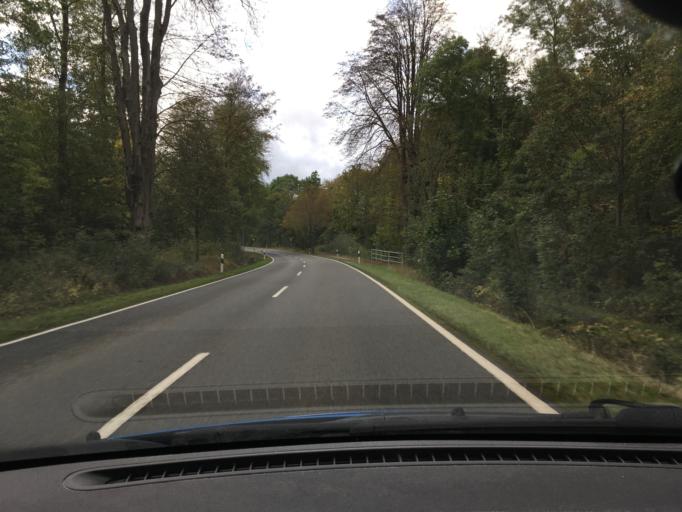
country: DE
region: Lower Saxony
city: Springe
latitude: 52.1876
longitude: 9.5830
